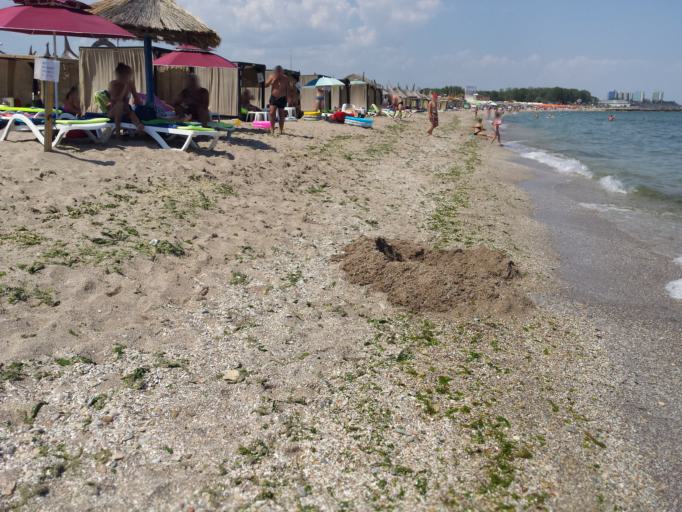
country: RO
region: Constanta
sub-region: Comuna Douazeci si Trei August
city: Douazeci si Trei August
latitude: 43.8624
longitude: 28.6064
